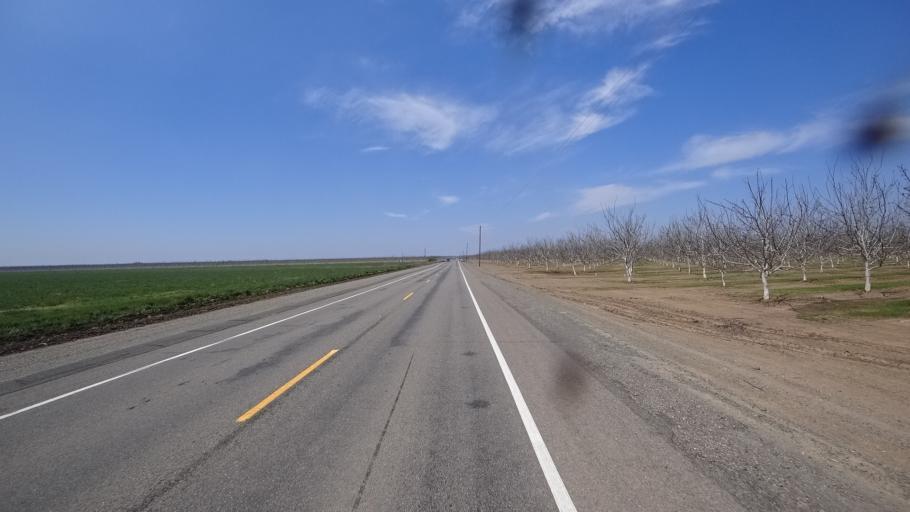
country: US
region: California
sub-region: Butte County
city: Durham
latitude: 39.4643
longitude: -121.9524
